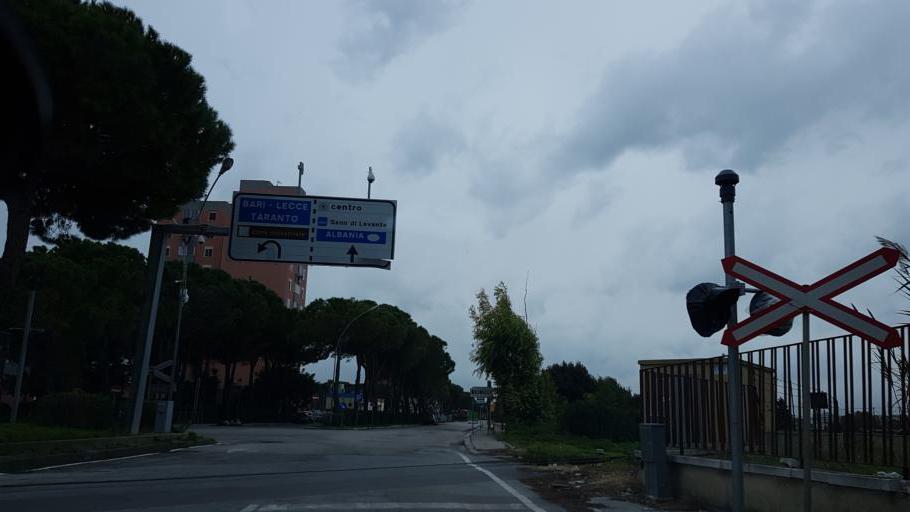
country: IT
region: Apulia
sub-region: Provincia di Brindisi
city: Brindisi
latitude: 40.6332
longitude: 17.9530
